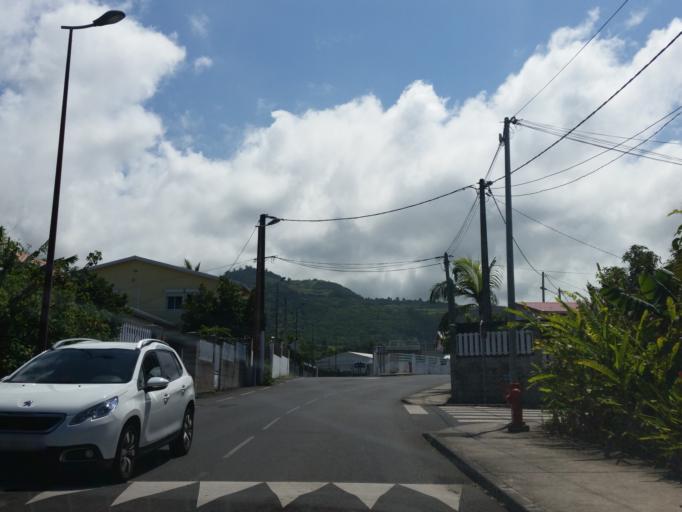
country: RE
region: Reunion
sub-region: Reunion
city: Saint-Joseph
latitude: -21.3793
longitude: 55.6100
